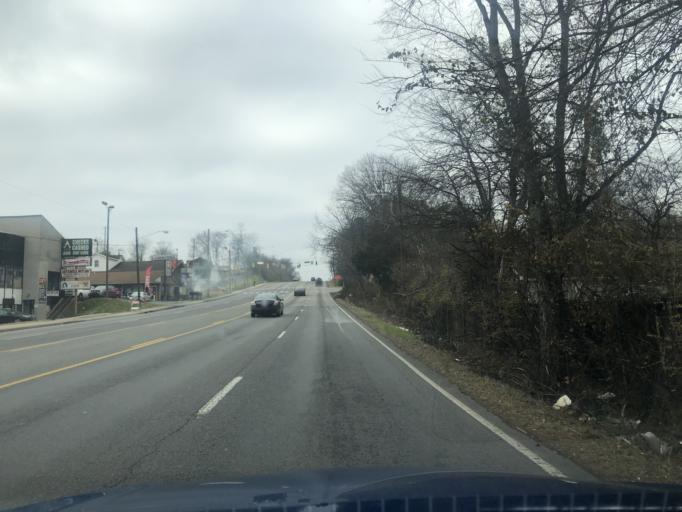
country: US
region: Tennessee
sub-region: Davidson County
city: Oak Hill
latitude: 36.0847
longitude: -86.7045
